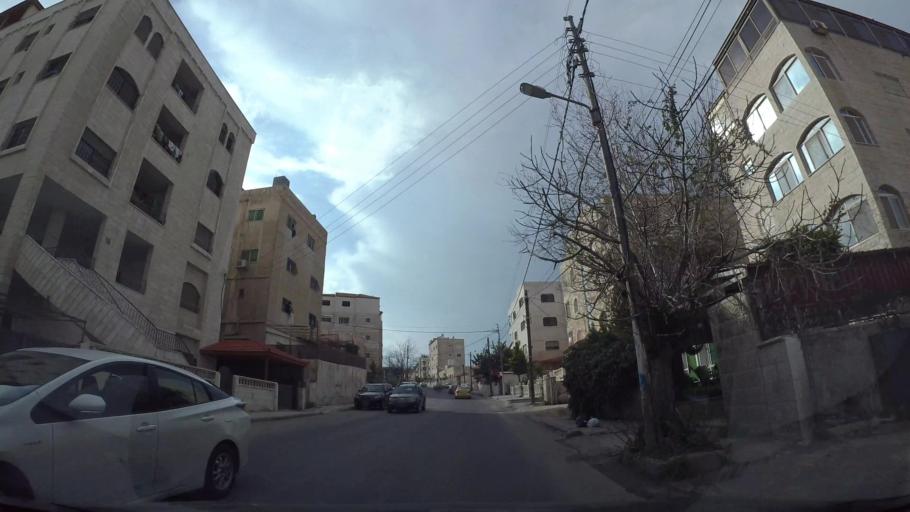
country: JO
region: Amman
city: Amman
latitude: 32.0008
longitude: 35.9459
